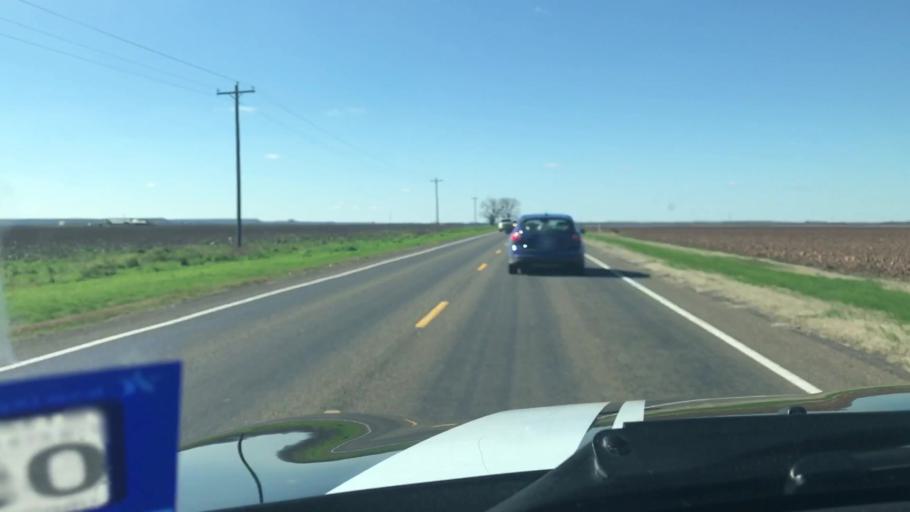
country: US
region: Texas
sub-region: Robertson County
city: Hearne
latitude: 30.8756
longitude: -96.6528
